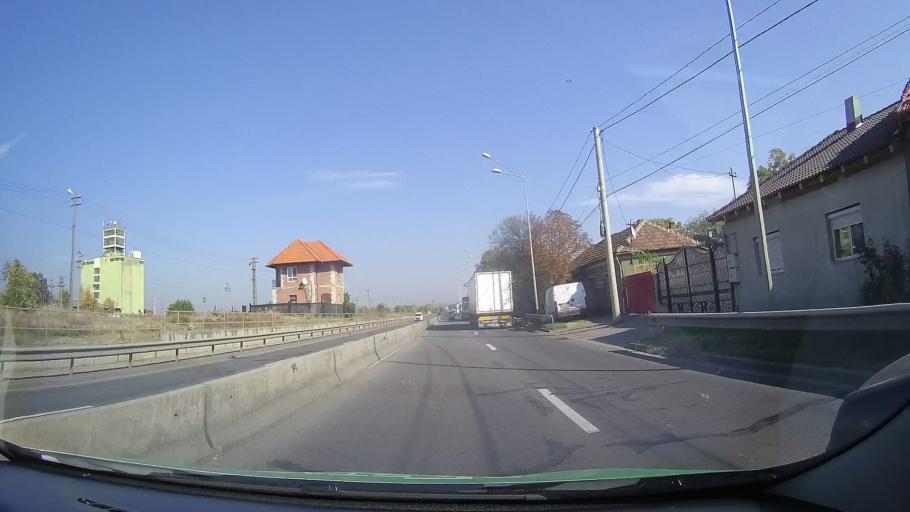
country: RO
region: Bihor
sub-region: Comuna Biharea
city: Oradea
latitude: 47.0628
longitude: 21.8966
